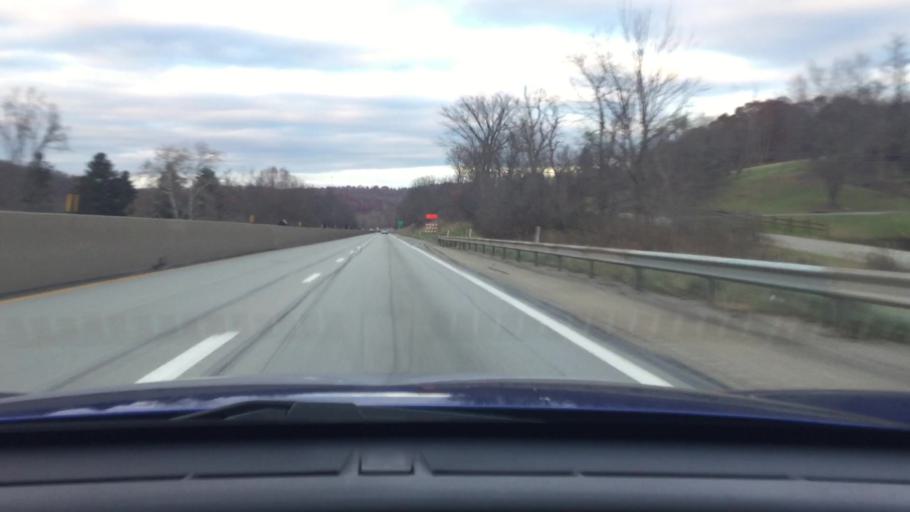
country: US
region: Pennsylvania
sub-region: Westmoreland County
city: New Stanton
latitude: 40.2008
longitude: -79.6820
